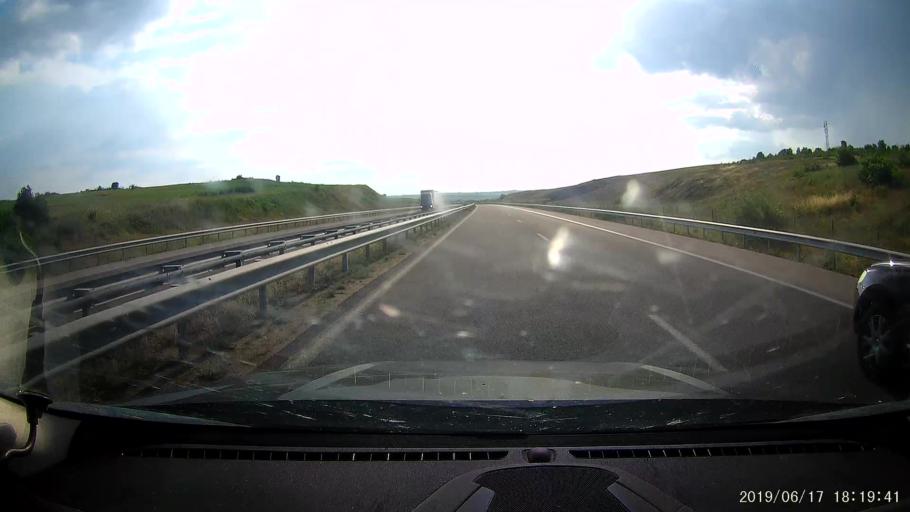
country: BG
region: Khaskovo
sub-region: Obshtina Kharmanli
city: Kharmanli
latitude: 41.9630
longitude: 25.8387
